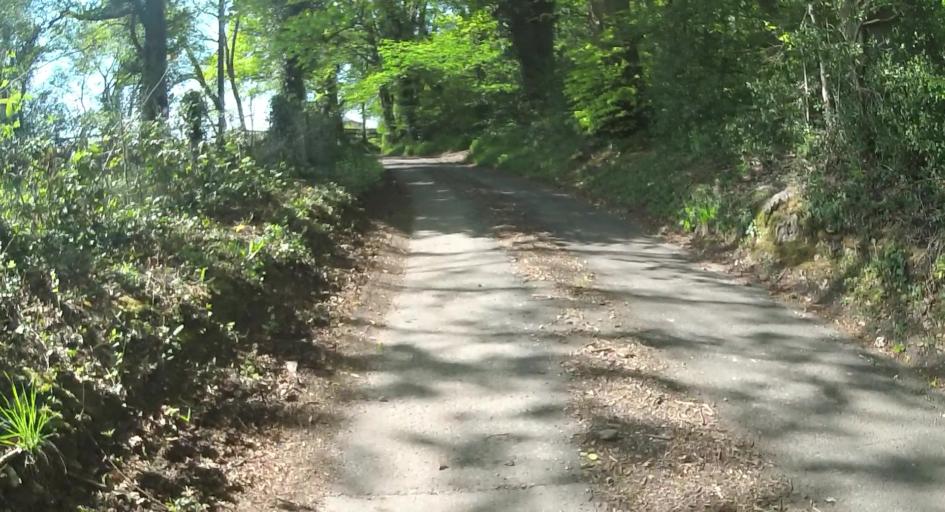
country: GB
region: England
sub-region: Hampshire
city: Alton
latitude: 51.1531
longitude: -1.0229
